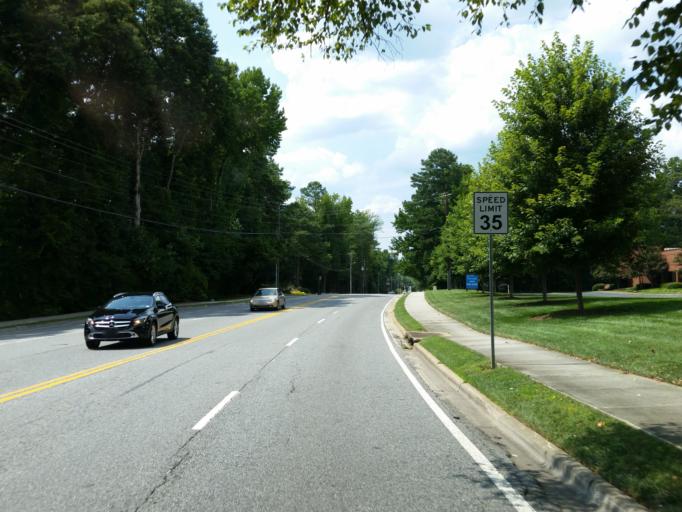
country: US
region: Georgia
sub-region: Fulton County
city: Roswell
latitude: 33.9907
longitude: -84.3438
